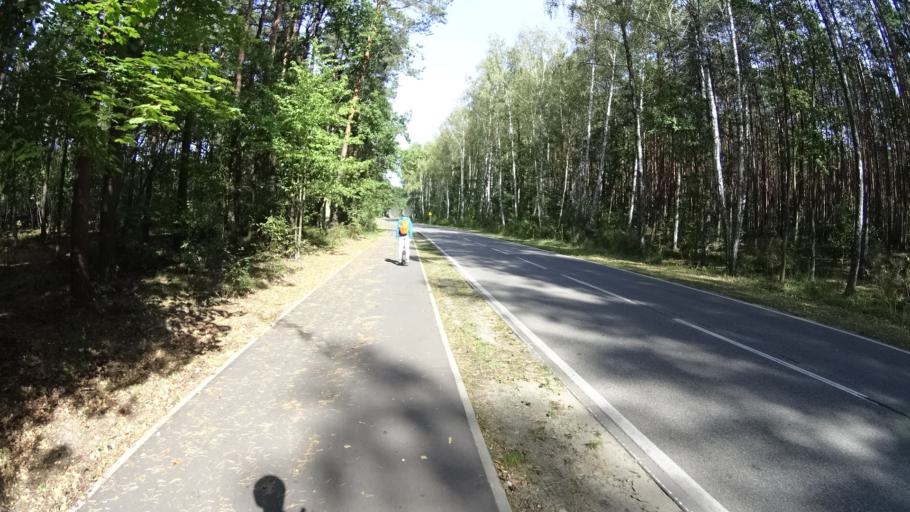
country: PL
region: Masovian Voivodeship
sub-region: Powiat legionowski
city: Bialobrzegi
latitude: 52.4553
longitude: 21.0731
